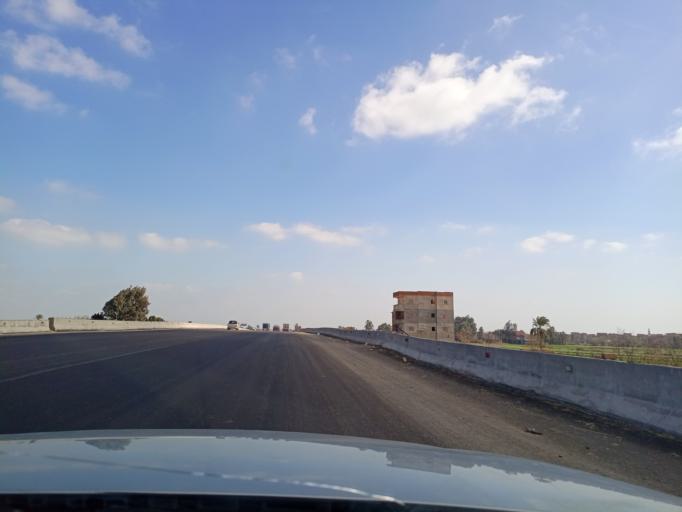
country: EG
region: Muhafazat al Minufiyah
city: Al Bajur
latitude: 30.4069
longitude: 31.0457
